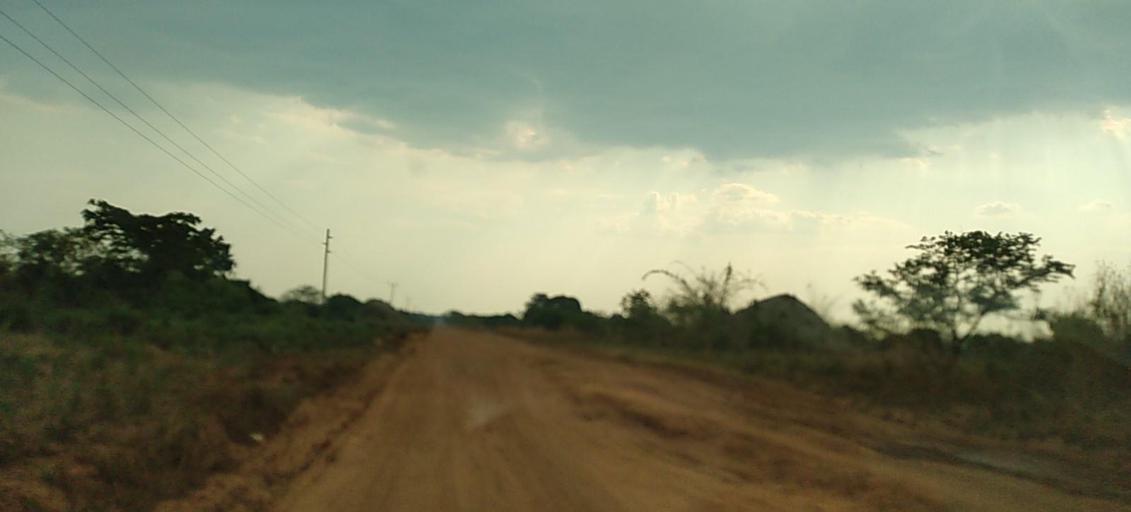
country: ZM
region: Copperbelt
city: Kalulushi
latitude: -12.9469
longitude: 27.9151
